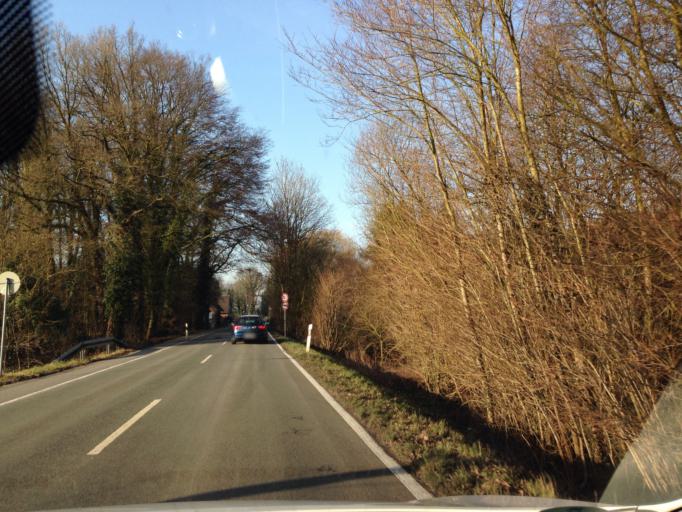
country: DE
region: North Rhine-Westphalia
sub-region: Regierungsbezirk Munster
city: Muenster
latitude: 52.0147
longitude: 7.6052
